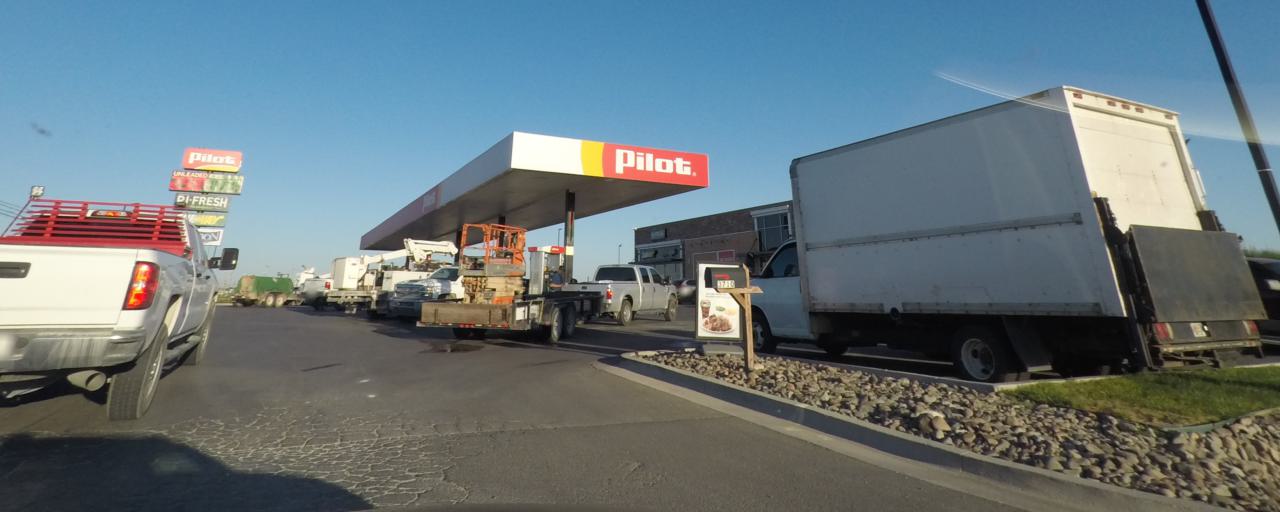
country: US
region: New Mexico
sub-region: Lea County
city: Hobbs
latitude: 32.6970
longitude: -103.1831
